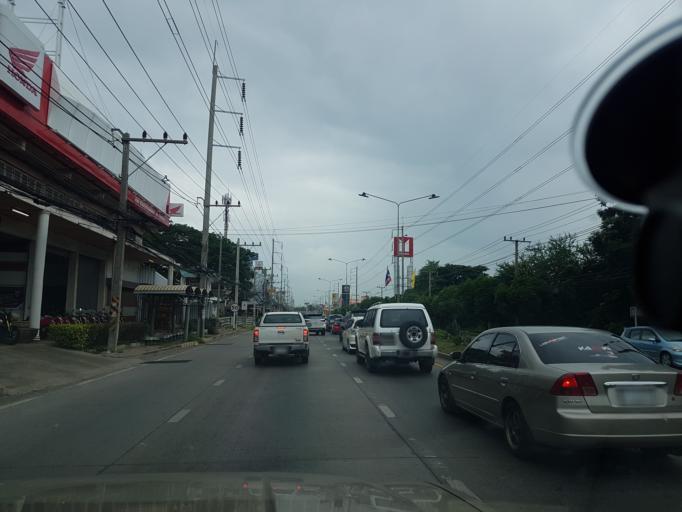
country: TH
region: Lop Buri
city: Lop Buri
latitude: 14.7956
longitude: 100.6662
